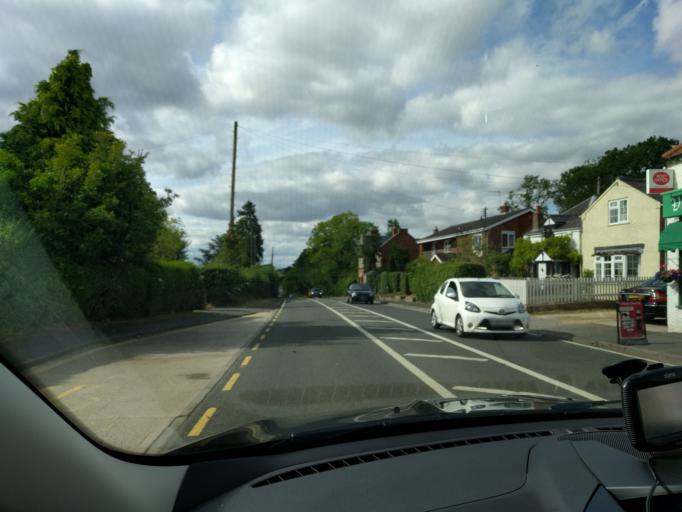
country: GB
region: England
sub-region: Warwickshire
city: Shipston on Stour
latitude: 52.1162
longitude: -1.6418
